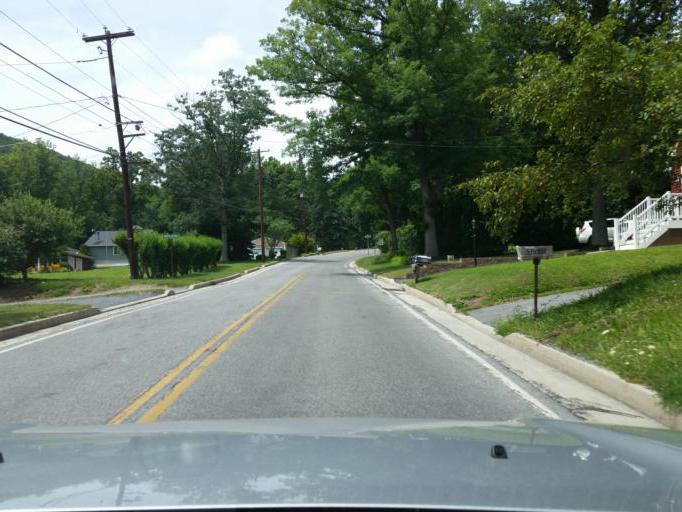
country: US
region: Pennsylvania
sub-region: Blair County
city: Altoona
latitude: 40.5526
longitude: -78.4399
